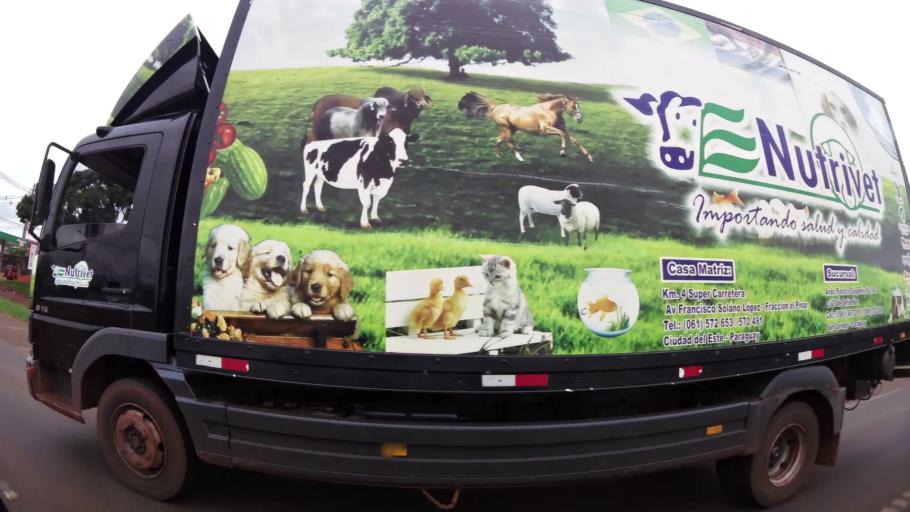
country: PY
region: Alto Parana
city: Presidente Franco
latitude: -25.4920
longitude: -54.7399
